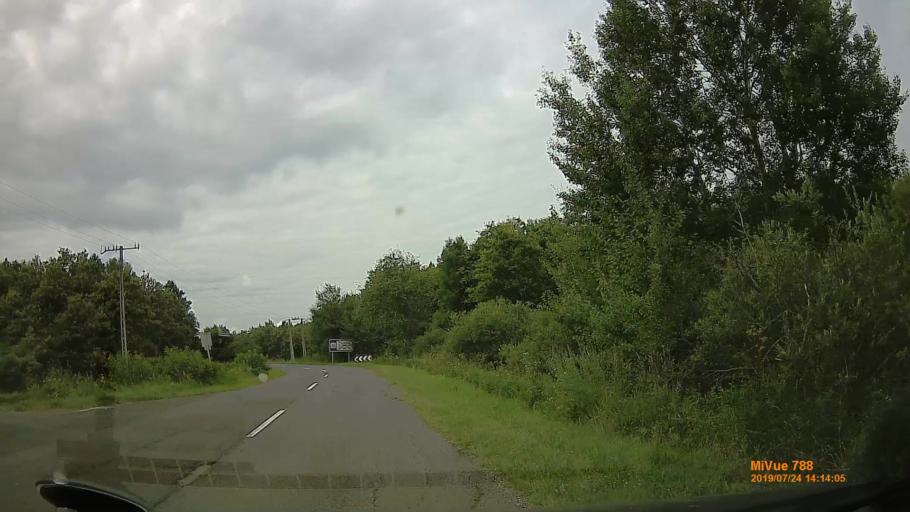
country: UA
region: Zakarpattia
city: Batiovo
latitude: 48.3203
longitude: 22.3162
